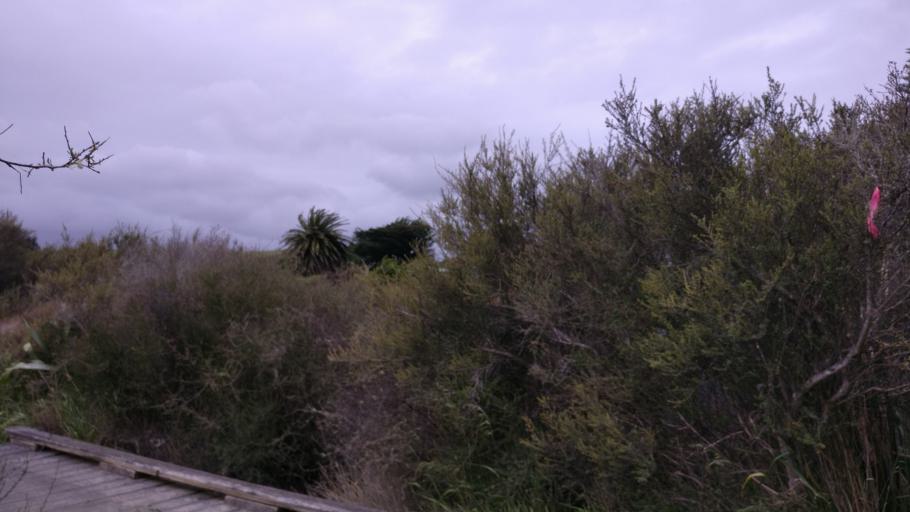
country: NZ
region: Wellington
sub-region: Porirua City
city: Porirua
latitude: -41.1038
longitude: 174.9156
